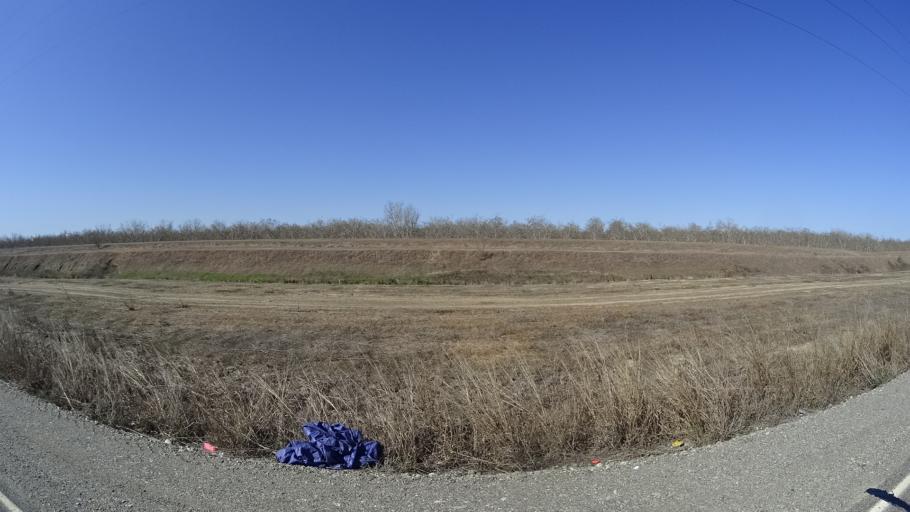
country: US
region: California
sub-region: Glenn County
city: Hamilton City
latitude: 39.7527
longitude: -122.0232
